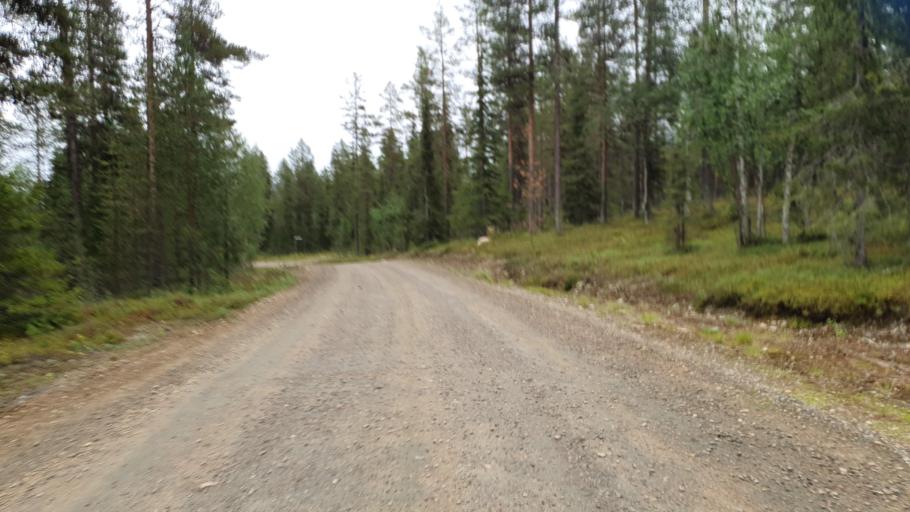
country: FI
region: Lapland
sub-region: Tunturi-Lappi
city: Kolari
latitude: 67.6004
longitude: 24.1940
